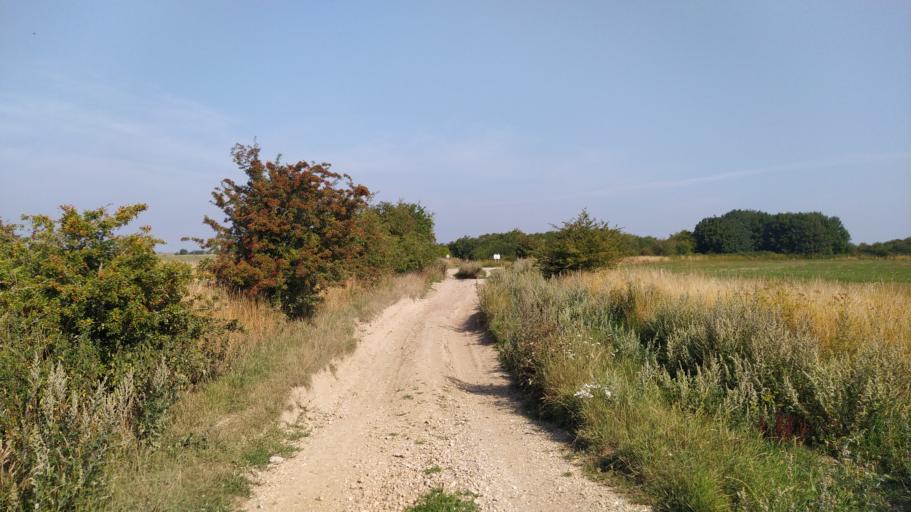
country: GB
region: England
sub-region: Wiltshire
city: Winterbourne Stoke
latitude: 51.1679
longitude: -1.9519
